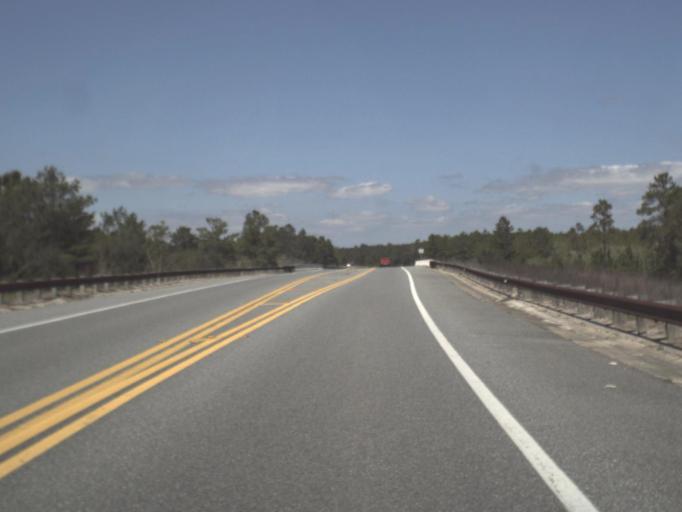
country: US
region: Florida
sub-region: Gulf County
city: Port Saint Joe
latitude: 29.8706
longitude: -85.3390
